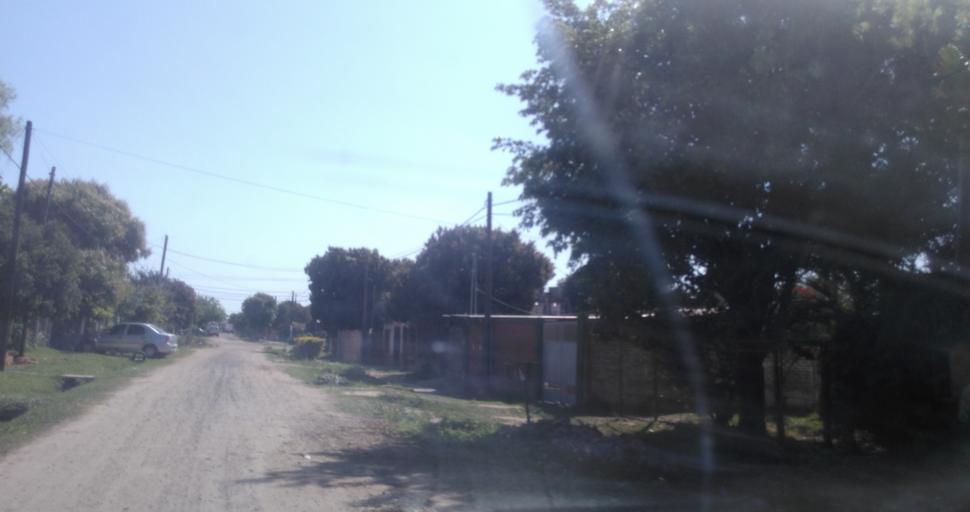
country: AR
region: Chaco
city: Fontana
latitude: -27.4236
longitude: -59.0154
